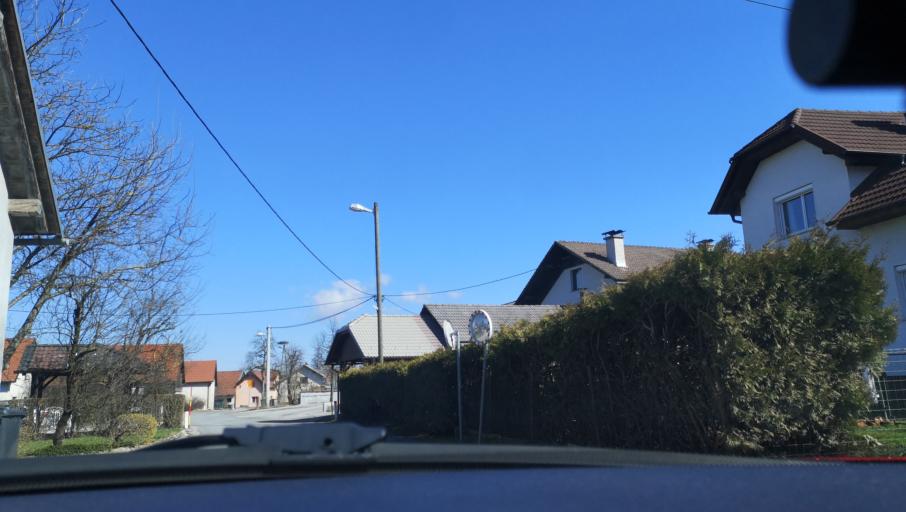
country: SI
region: Ig
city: Ig
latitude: 45.9577
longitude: 14.5141
